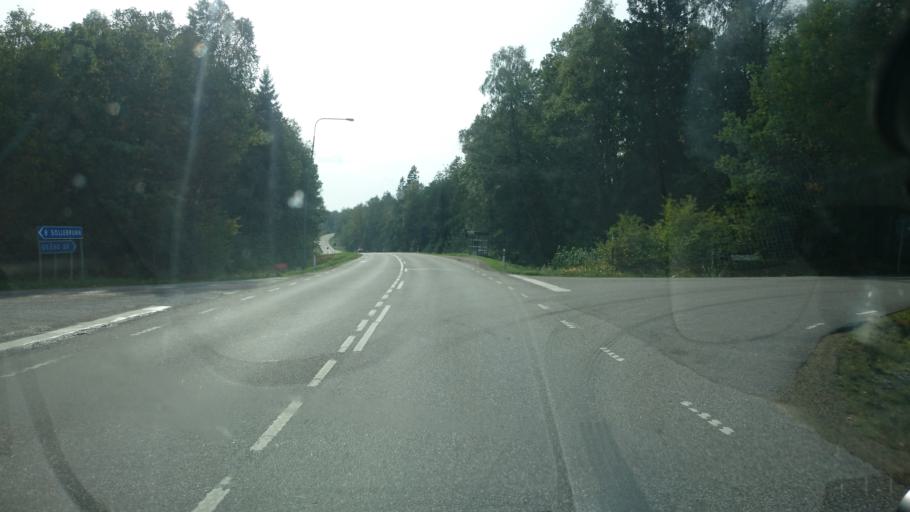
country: SE
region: Vaestra Goetaland
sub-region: Alingsas Kommun
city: Sollebrunn
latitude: 58.0559
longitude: 12.4656
